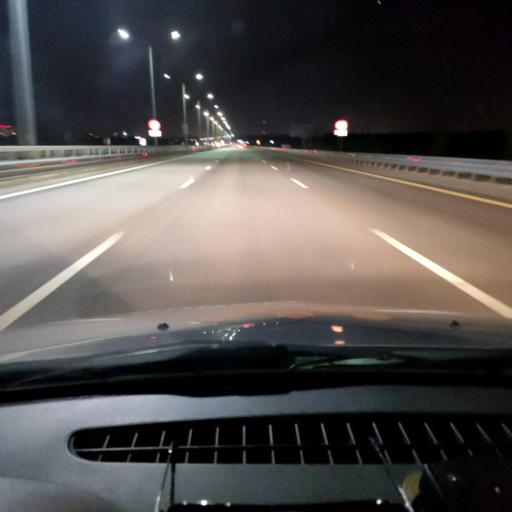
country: RU
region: Voronezj
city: Somovo
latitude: 51.7558
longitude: 39.3066
